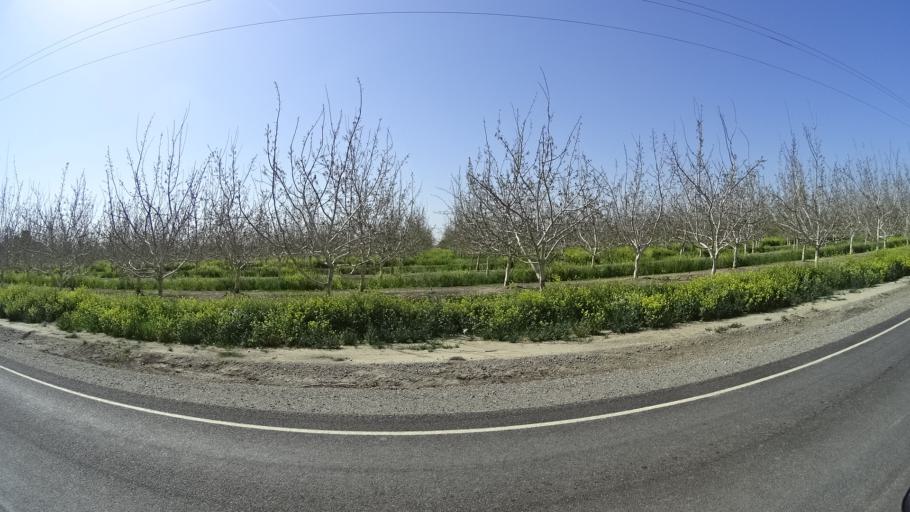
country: US
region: California
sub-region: Glenn County
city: Hamilton City
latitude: 39.6597
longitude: -122.0603
